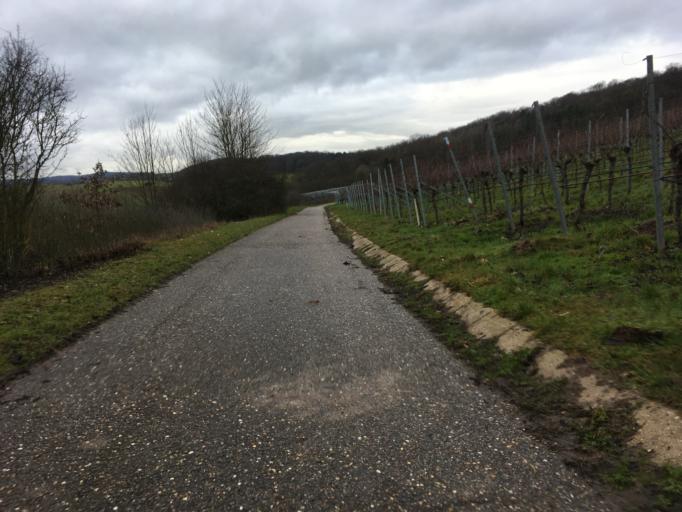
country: DE
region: Baden-Wuerttemberg
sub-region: Regierungsbezirk Stuttgart
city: Schwaigern
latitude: 49.1409
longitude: 9.0257
